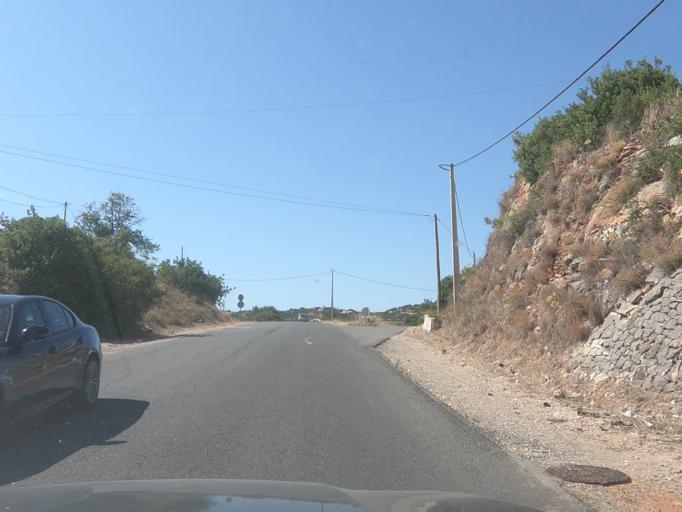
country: PT
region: Faro
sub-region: Faro
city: Santa Barbara de Nexe
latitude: 37.0928
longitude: -7.9960
